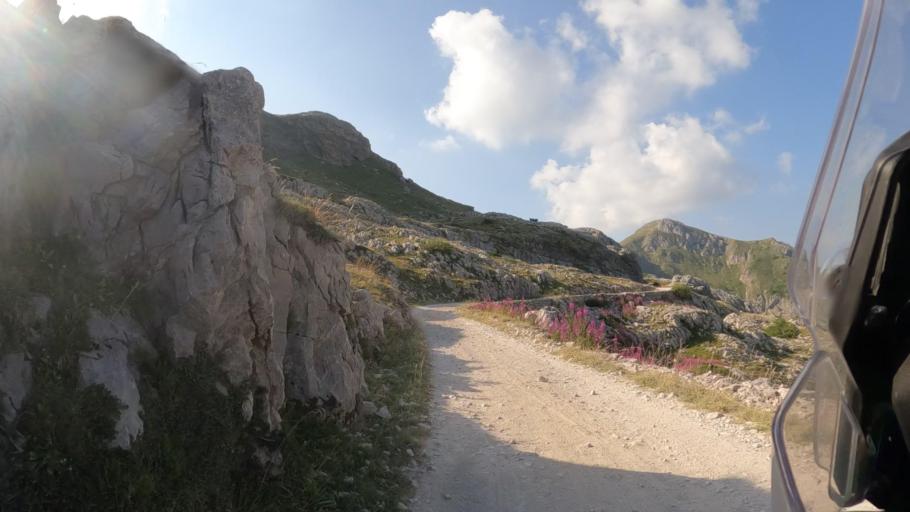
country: IT
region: Piedmont
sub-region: Provincia di Cuneo
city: Limone Piemonte
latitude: 44.1641
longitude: 7.6695
